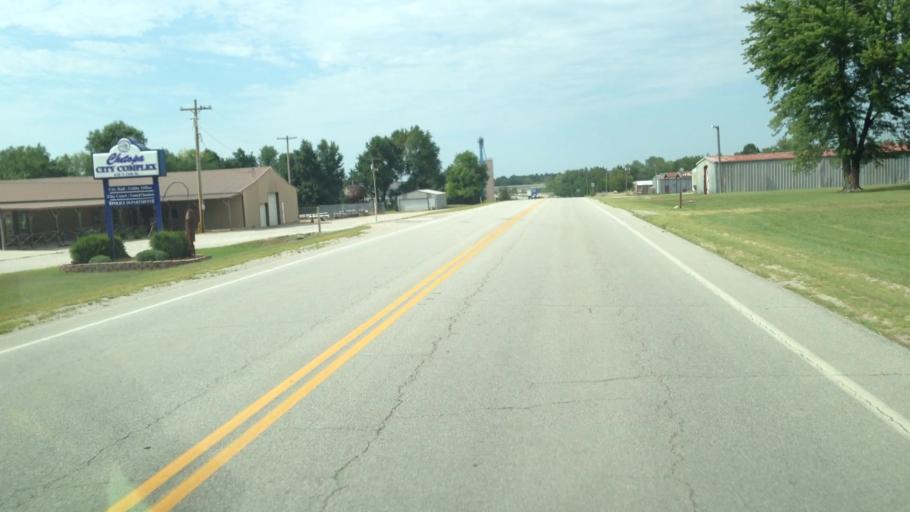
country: US
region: Kansas
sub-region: Labette County
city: Chetopa
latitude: 37.0425
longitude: -95.1002
